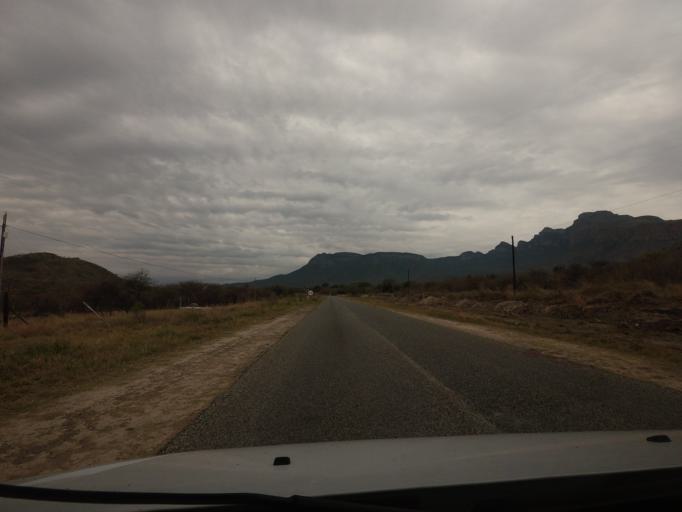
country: ZA
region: Limpopo
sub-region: Mopani District Municipality
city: Hoedspruit
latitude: -24.4961
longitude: 30.8926
